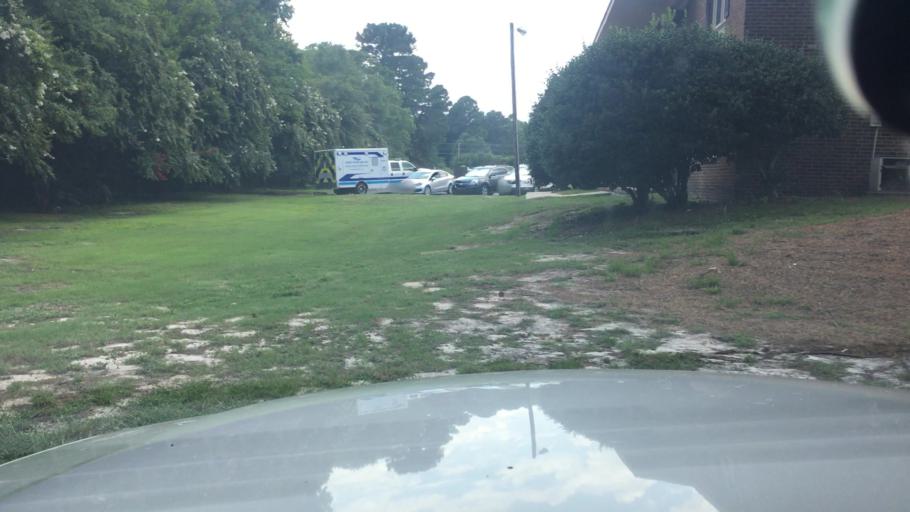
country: US
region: North Carolina
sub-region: Cumberland County
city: Fayetteville
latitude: 35.0263
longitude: -78.9226
